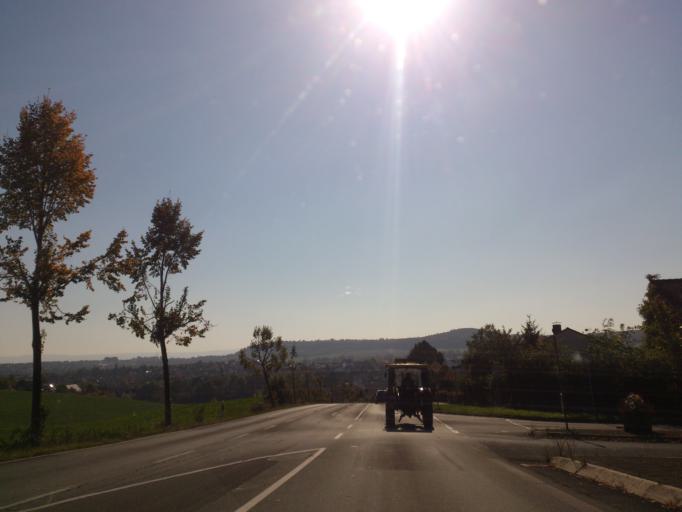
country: DE
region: Hesse
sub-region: Regierungsbezirk Kassel
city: Calden
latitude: 51.3731
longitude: 9.4165
